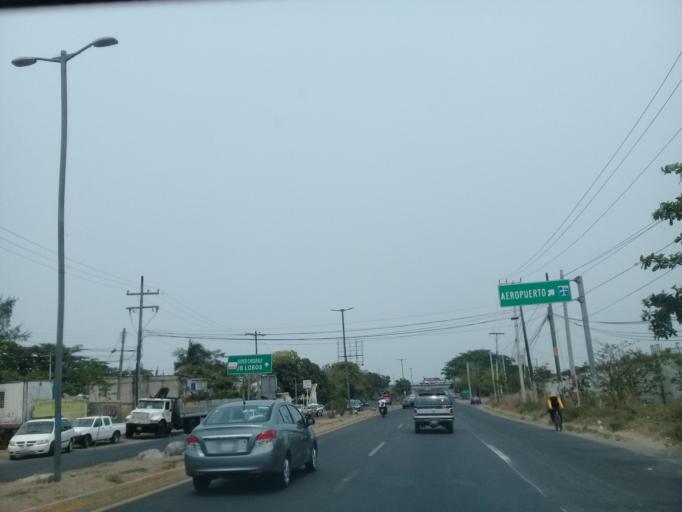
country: MX
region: Veracruz
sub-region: Veracruz
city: Hacienda Sotavento
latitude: 19.1511
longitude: -96.1773
